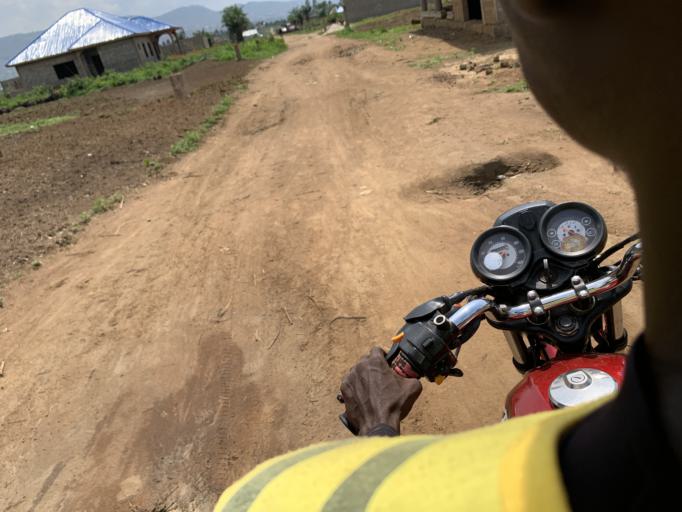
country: SL
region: Western Area
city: Waterloo
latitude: 8.3559
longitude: -13.0450
